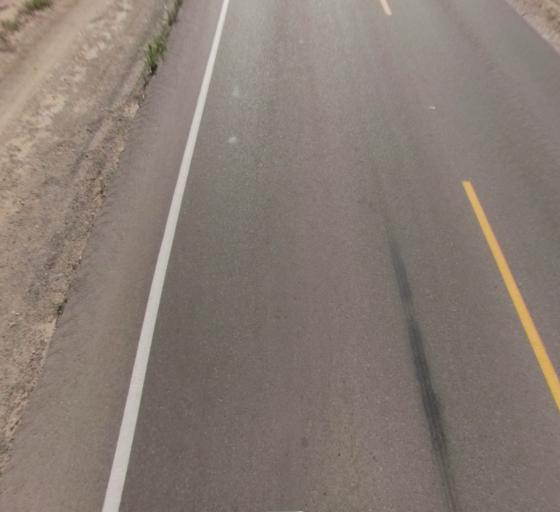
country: US
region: California
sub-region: Fresno County
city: Biola
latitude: 36.8517
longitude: -120.0167
